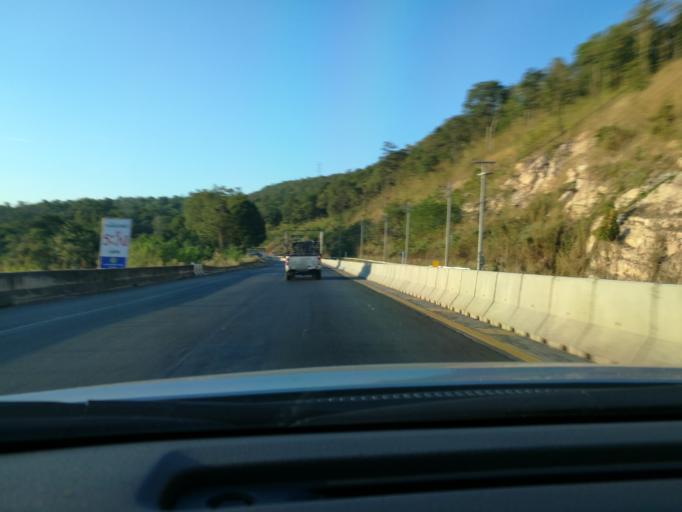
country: TH
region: Phitsanulok
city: Wang Thong
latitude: 16.8518
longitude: 100.5157
